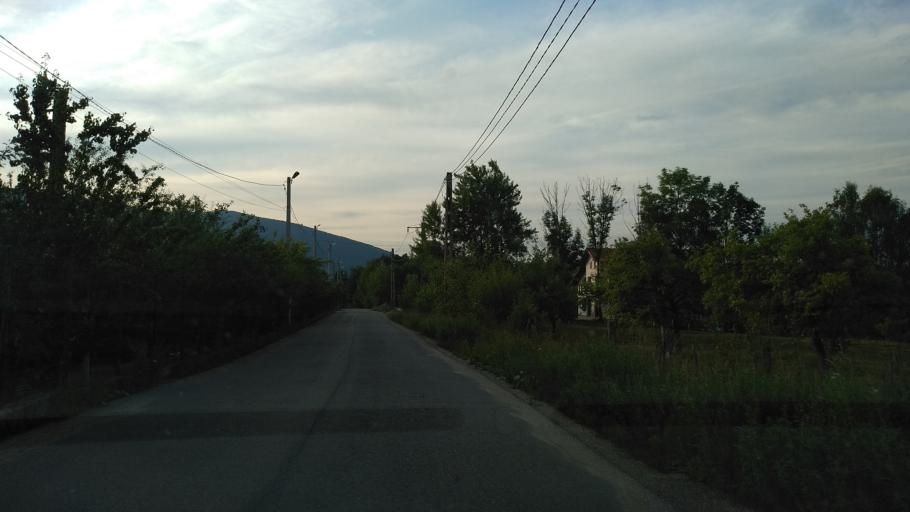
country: RO
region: Hunedoara
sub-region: Municipiul  Vulcan
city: Jiu-Paroseni
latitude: 45.3585
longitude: 23.2880
